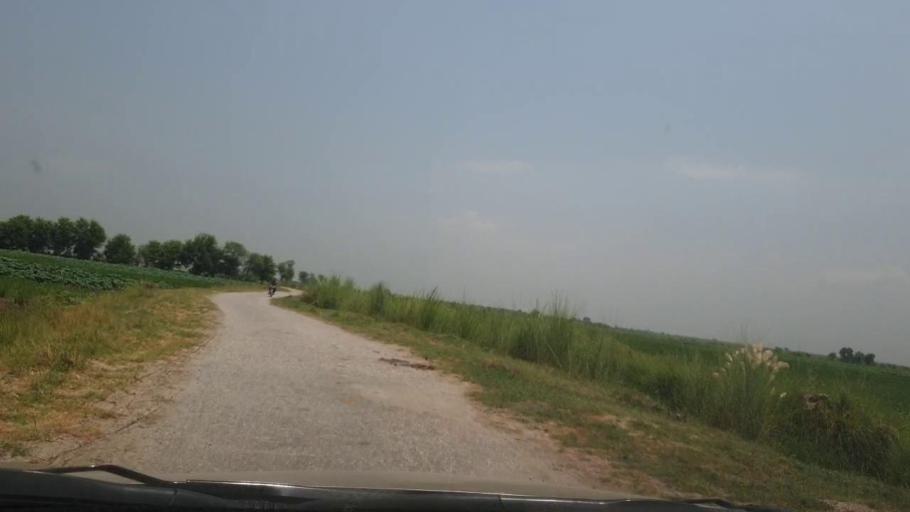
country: PK
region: Sindh
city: Ratodero
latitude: 27.7324
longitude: 68.3105
